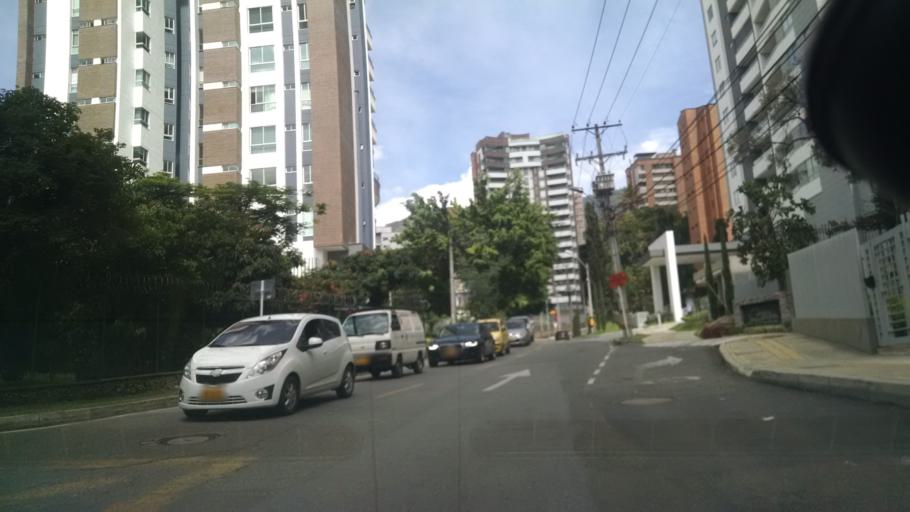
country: CO
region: Antioquia
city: Medellin
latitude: 6.2143
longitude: -75.5680
